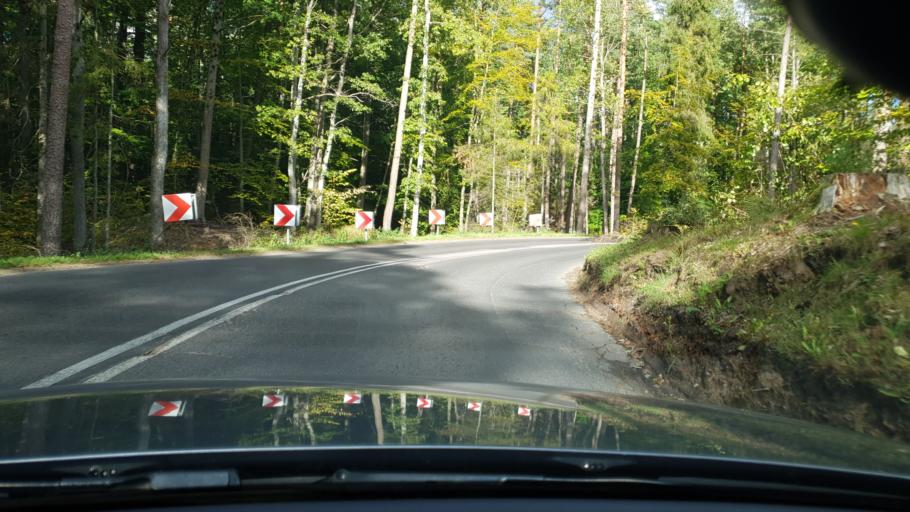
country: PL
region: Pomeranian Voivodeship
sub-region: Powiat wejherowski
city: Koleczkowo
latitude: 54.4984
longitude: 18.3614
